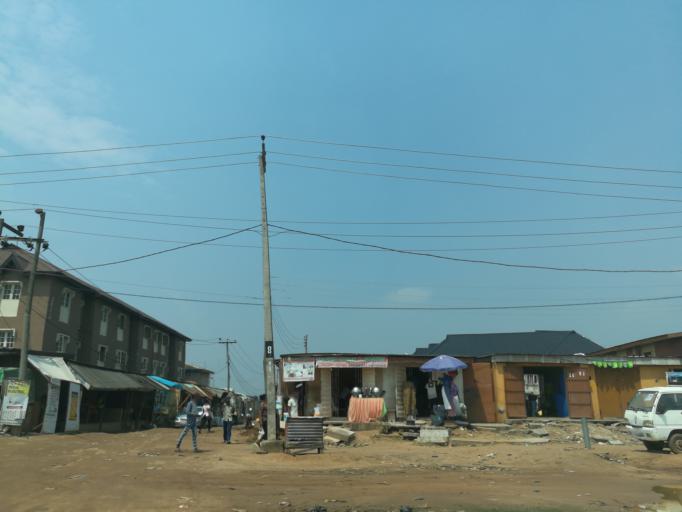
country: NG
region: Lagos
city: Ikorodu
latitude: 6.6385
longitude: 3.4814
